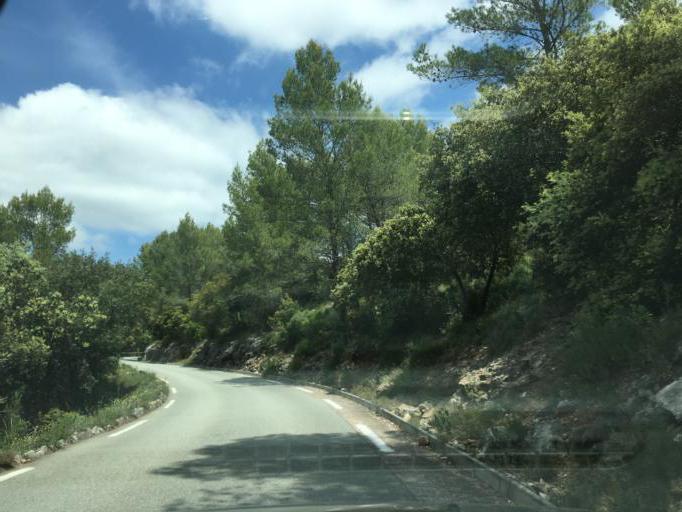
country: FR
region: Provence-Alpes-Cote d'Azur
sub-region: Departement du Var
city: Taradeau
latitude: 43.4568
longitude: 6.4319
